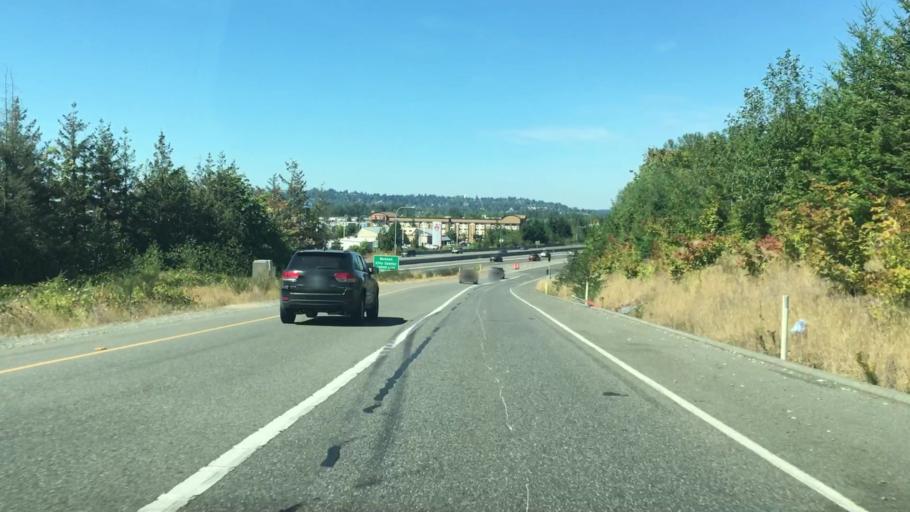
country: US
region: Washington
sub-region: King County
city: Renton
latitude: 47.4426
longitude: -122.2162
